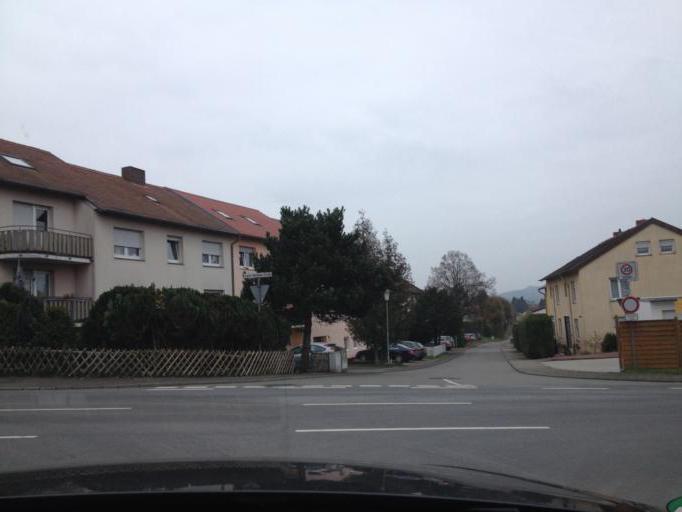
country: DE
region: Saarland
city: Sankt Wendel
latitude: 49.4678
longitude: 7.1493
